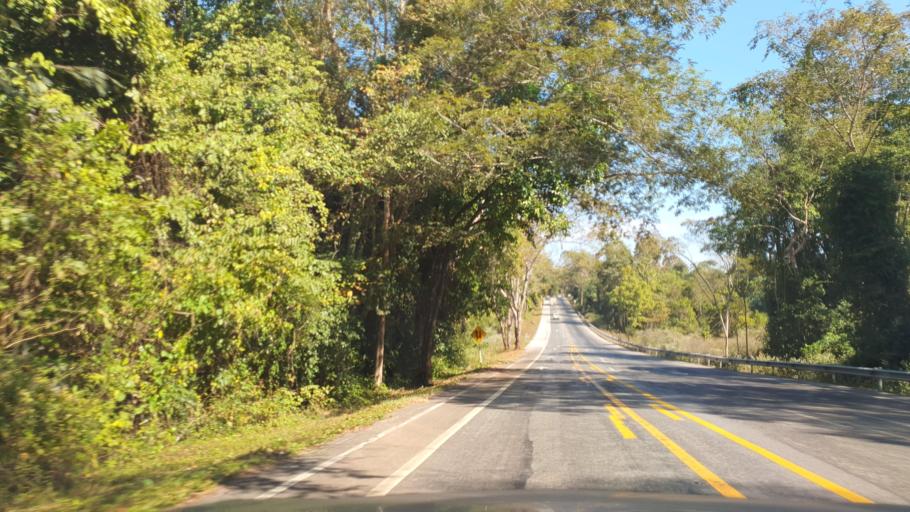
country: TH
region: Kalasin
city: Na Khu
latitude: 16.8478
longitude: 103.9218
